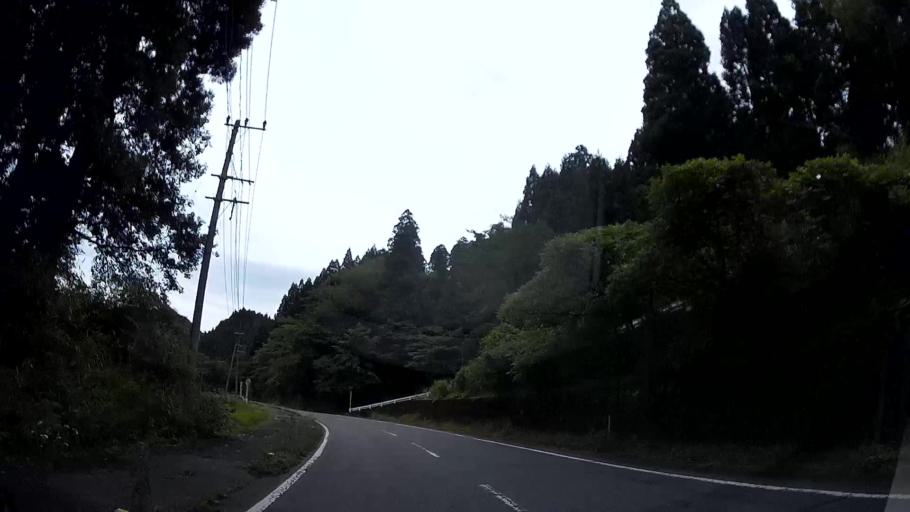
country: JP
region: Oita
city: Hita
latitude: 33.1267
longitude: 130.9975
